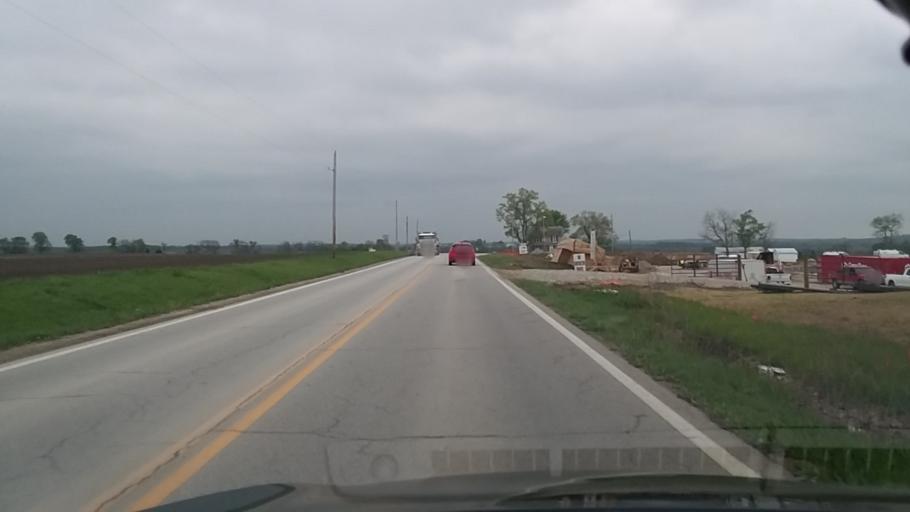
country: US
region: Kansas
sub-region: Douglas County
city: Eudora
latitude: 38.9149
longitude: -95.0935
